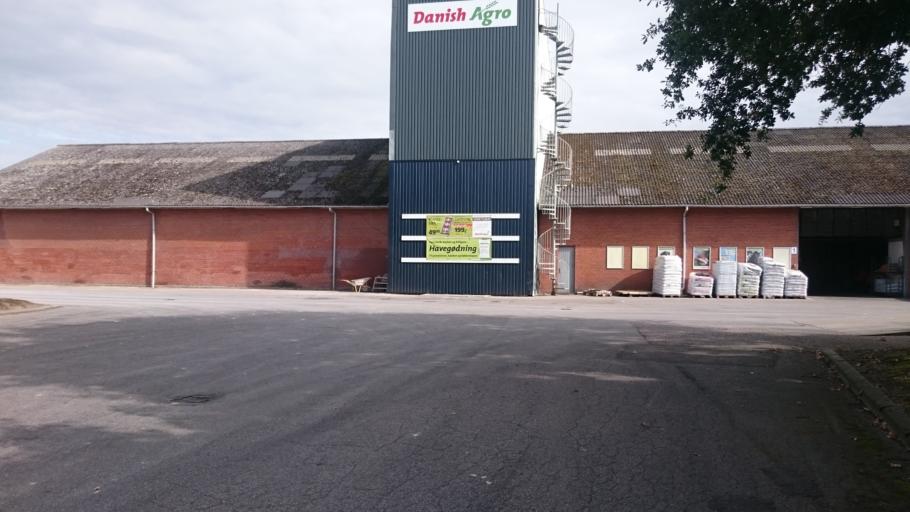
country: DK
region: South Denmark
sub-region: Esbjerg Kommune
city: Ribe
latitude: 55.3043
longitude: 8.7679
